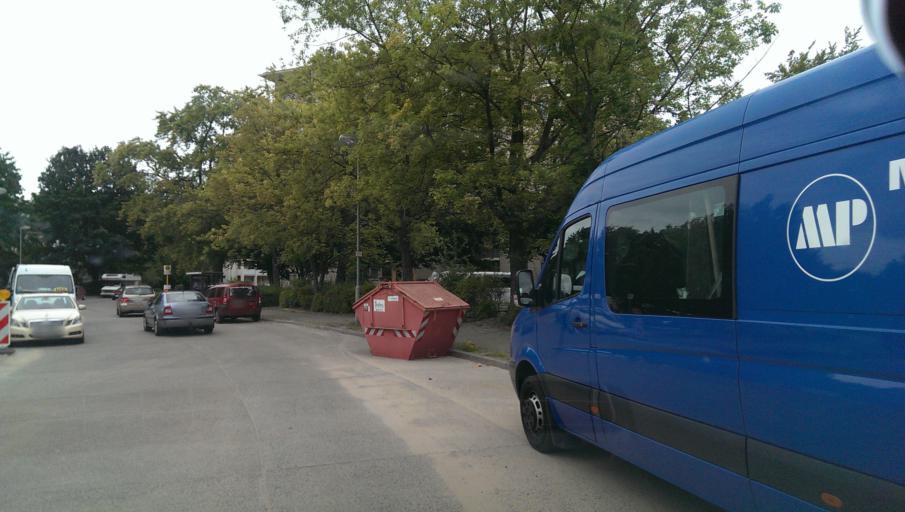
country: DE
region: Berlin
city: Tempelhof Bezirk
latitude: 52.4449
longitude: 13.4077
